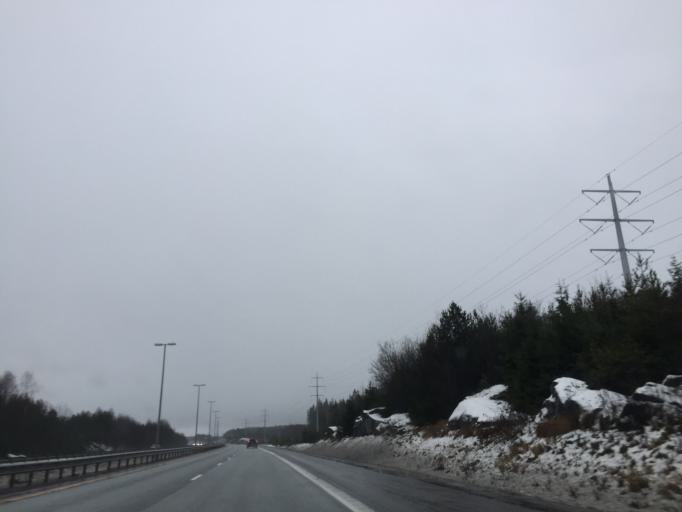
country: NO
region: Akershus
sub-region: Vestby
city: Vestby
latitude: 59.5640
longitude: 10.7208
